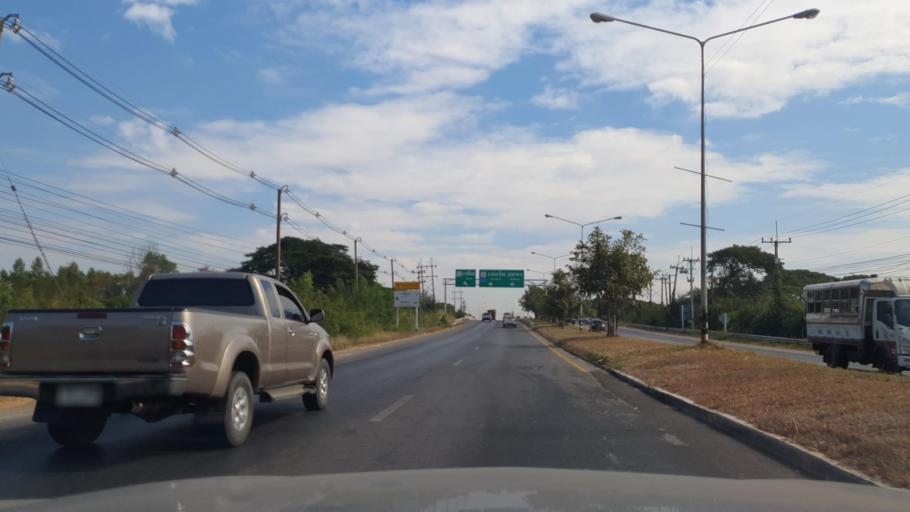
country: TH
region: Kalasin
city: Kalasin
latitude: 16.4108
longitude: 103.4650
